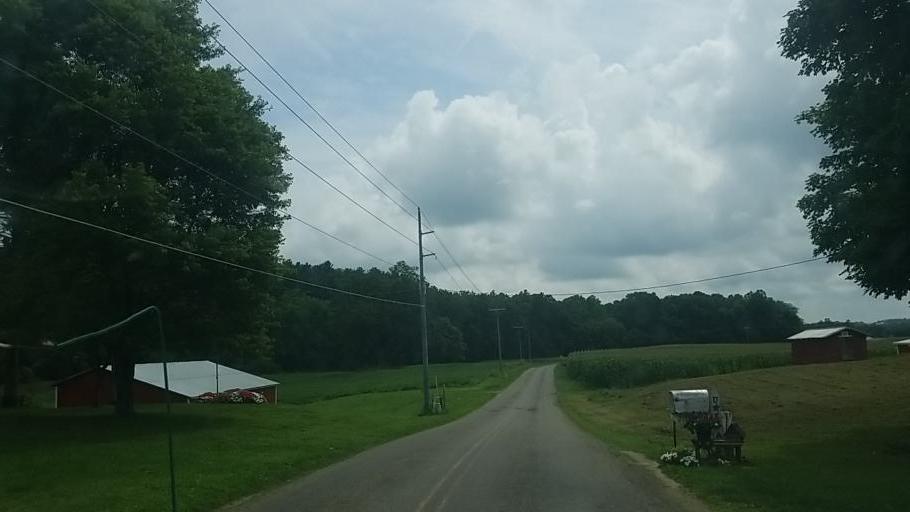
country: US
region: Ohio
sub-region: Knox County
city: Gambier
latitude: 40.3946
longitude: -82.3561
